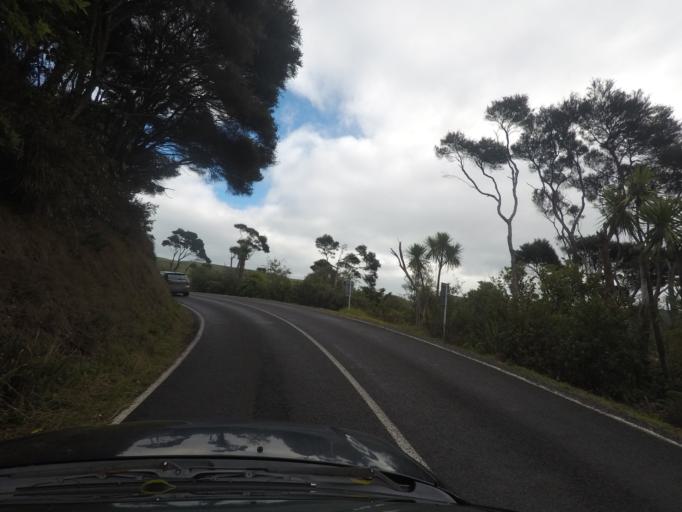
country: NZ
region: Auckland
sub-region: Auckland
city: Muriwai Beach
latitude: -36.8769
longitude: 174.4556
